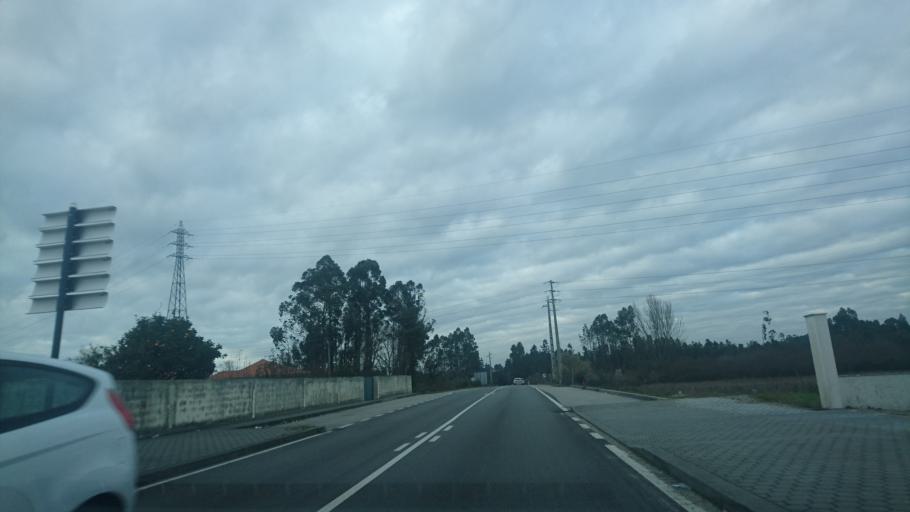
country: PT
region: Aveiro
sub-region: Santa Maria da Feira
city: Rio Meao
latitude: 40.9590
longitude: -8.5893
